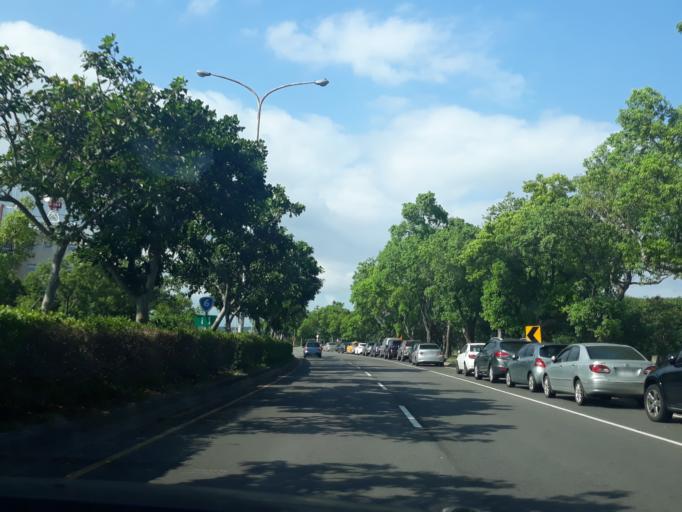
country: TW
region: Taiwan
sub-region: Miaoli
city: Miaoli
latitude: 24.5805
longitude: 120.8432
